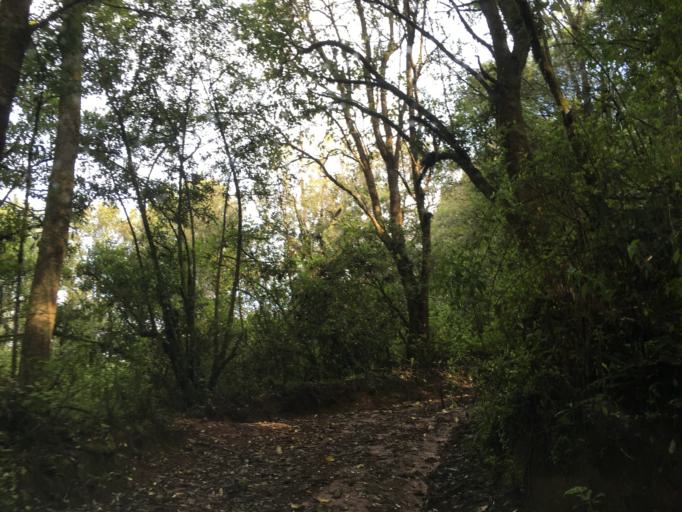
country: MX
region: Michoacan
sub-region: Zitacuaro
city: Francisco Serrato (San Bartolo)
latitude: 19.5154
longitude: -100.3032
